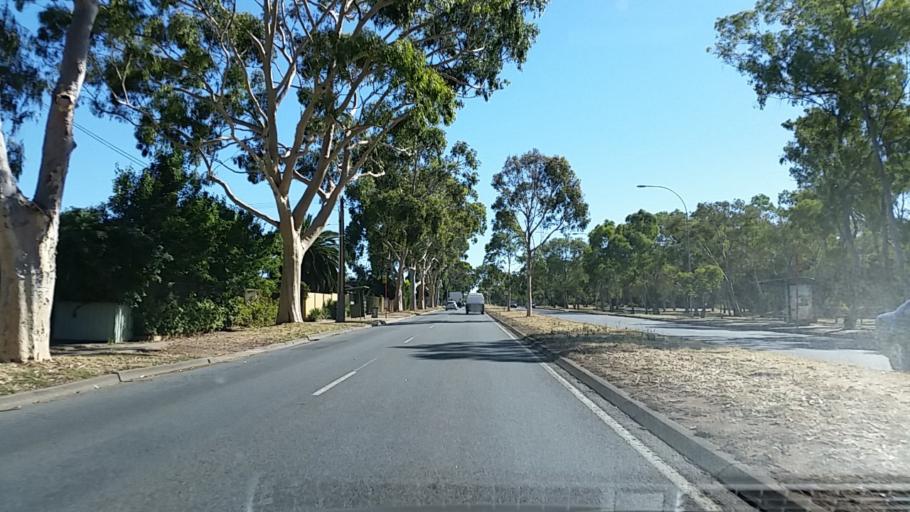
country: AU
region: South Australia
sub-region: Salisbury
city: Ingle Farm
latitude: -34.8116
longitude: 138.6449
